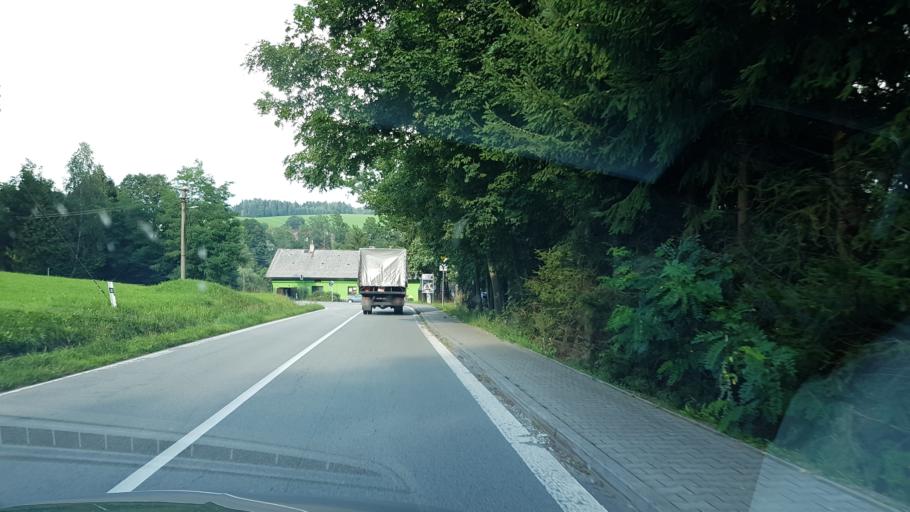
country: CZ
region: Pardubicky
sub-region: Okres Usti nad Orlici
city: Kunvald
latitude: 50.0911
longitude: 16.5603
